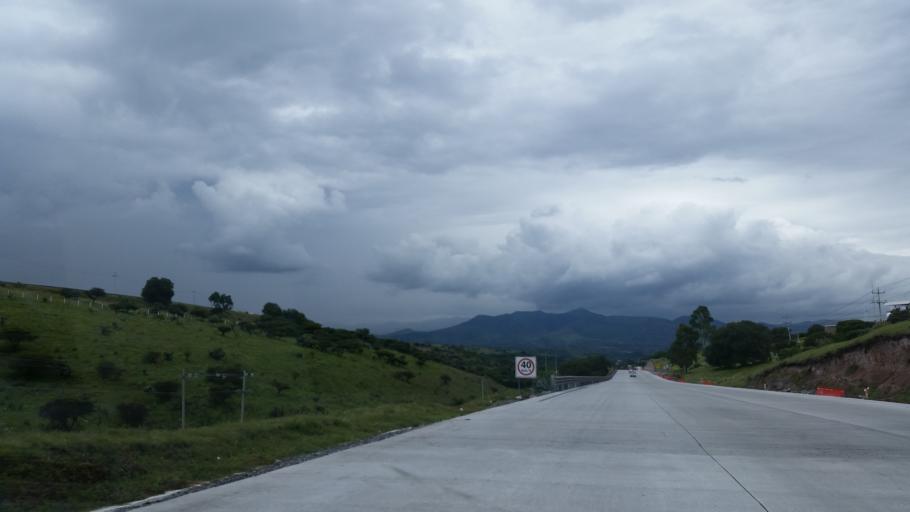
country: MX
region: Hidalgo
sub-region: Tepeji del Rio de Ocampo
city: Cantera de Villagran
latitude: 19.8580
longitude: -99.2976
